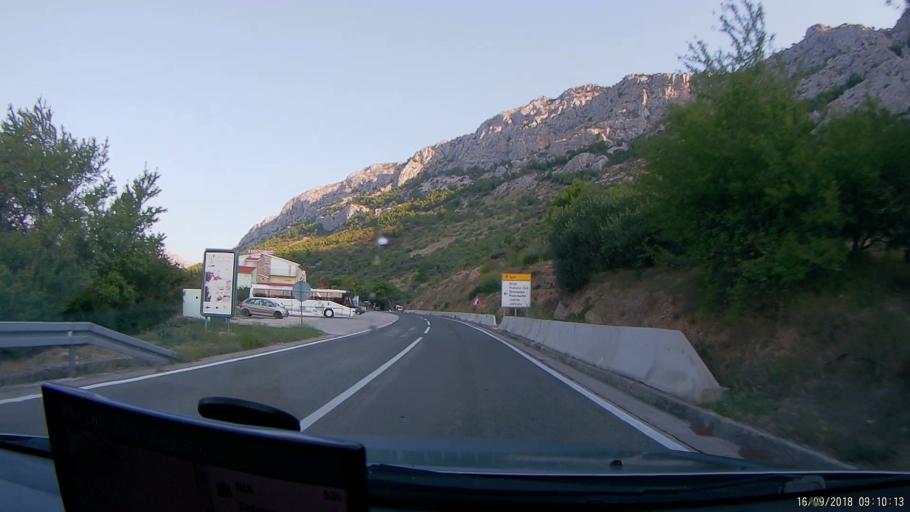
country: HR
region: Splitsko-Dalmatinska
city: Donja Brela
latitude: 43.3799
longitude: 16.9217
